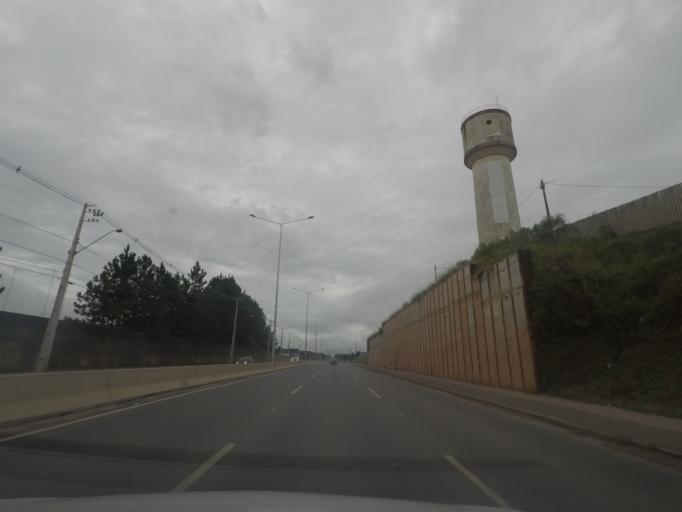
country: BR
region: Parana
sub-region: Piraquara
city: Piraquara
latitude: -25.4500
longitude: -49.1264
